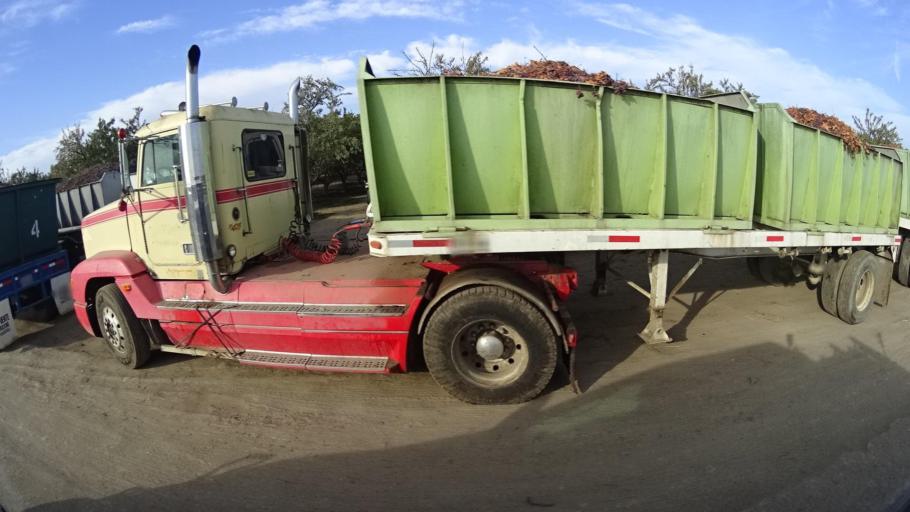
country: US
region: California
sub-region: Kern County
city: Delano
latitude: 35.7857
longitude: -119.2053
